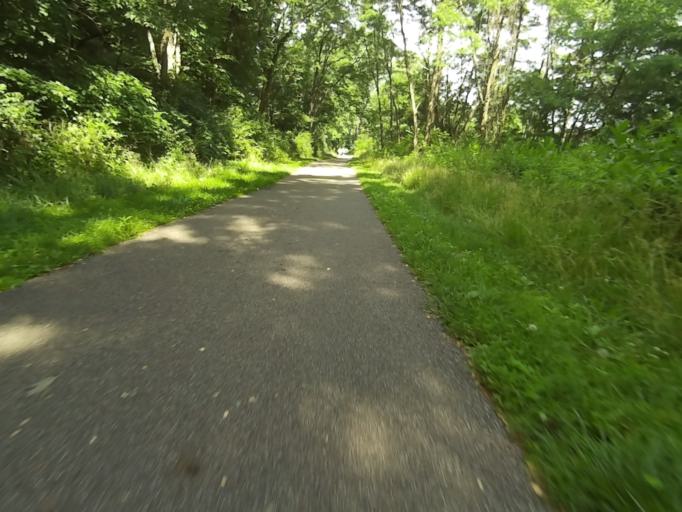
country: US
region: Ohio
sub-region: Summit County
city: Stow
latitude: 41.1971
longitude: -81.4283
